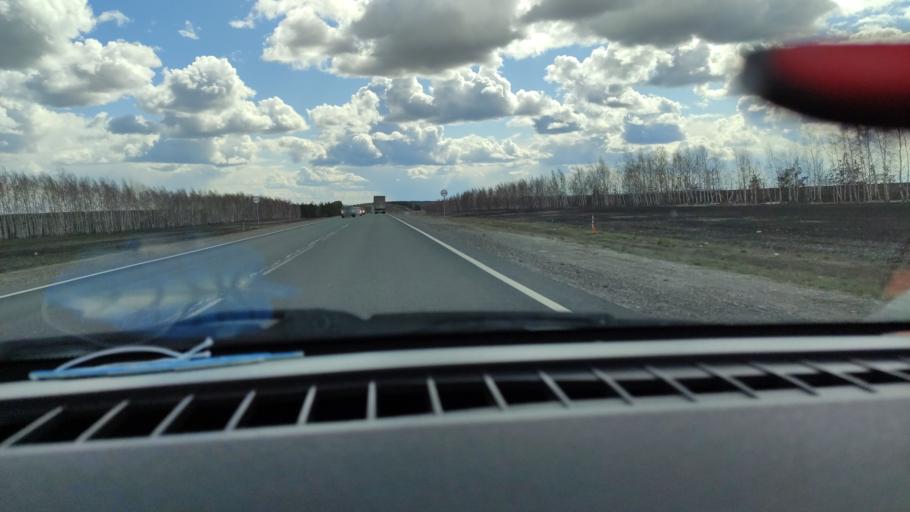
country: RU
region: Samara
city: Syzran'
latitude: 52.9027
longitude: 48.2971
